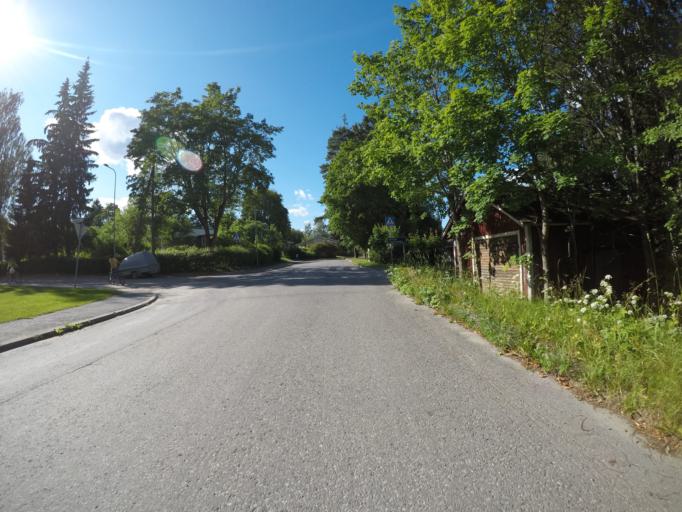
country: FI
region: Haeme
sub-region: Haemeenlinna
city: Haemeenlinna
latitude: 61.0050
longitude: 24.4988
